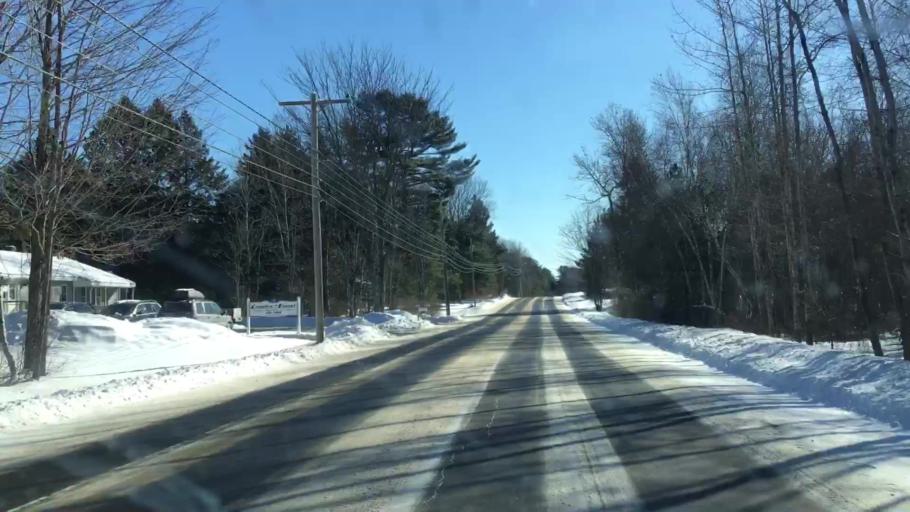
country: US
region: Maine
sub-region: Sagadahoc County
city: Topsham
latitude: 43.9068
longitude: -70.0057
